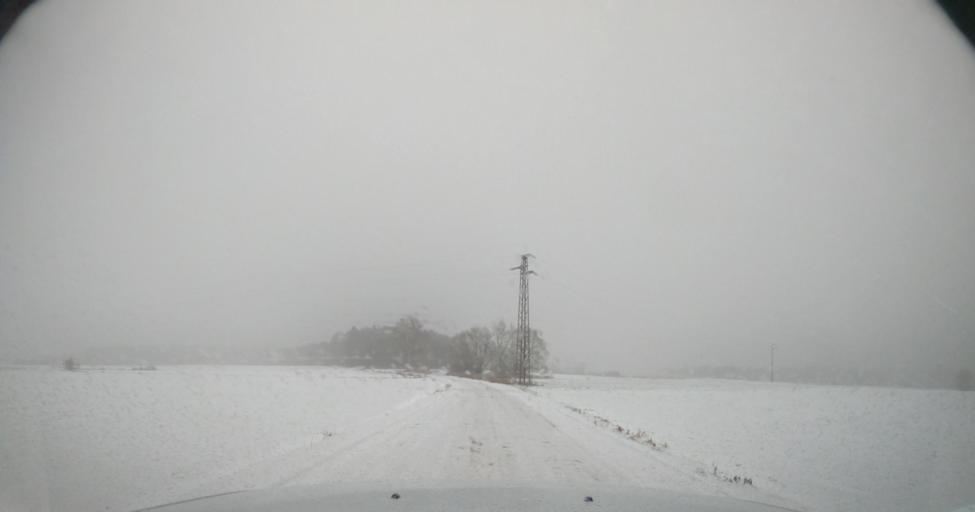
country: PL
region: West Pomeranian Voivodeship
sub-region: Powiat kamienski
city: Golczewo
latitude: 53.7684
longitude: 14.9151
